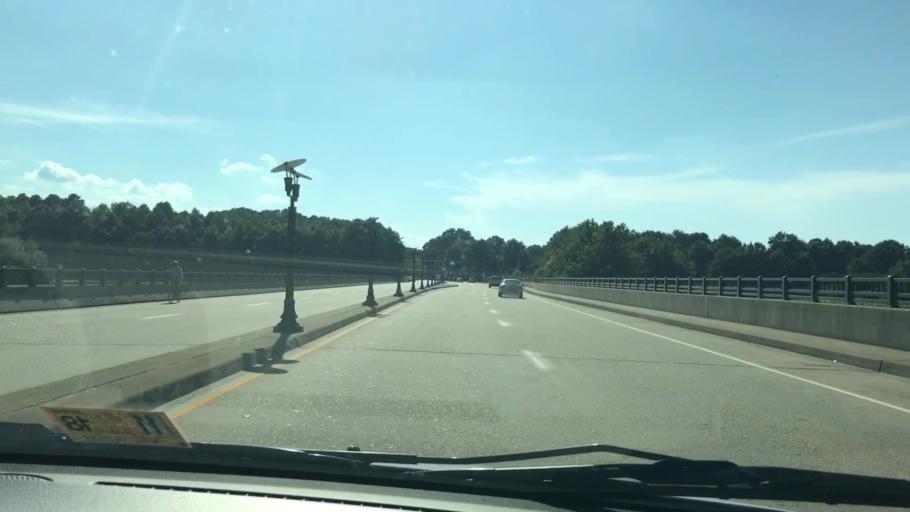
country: US
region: Virginia
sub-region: City of Norfolk
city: Norfolk
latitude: 36.8982
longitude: -76.2125
